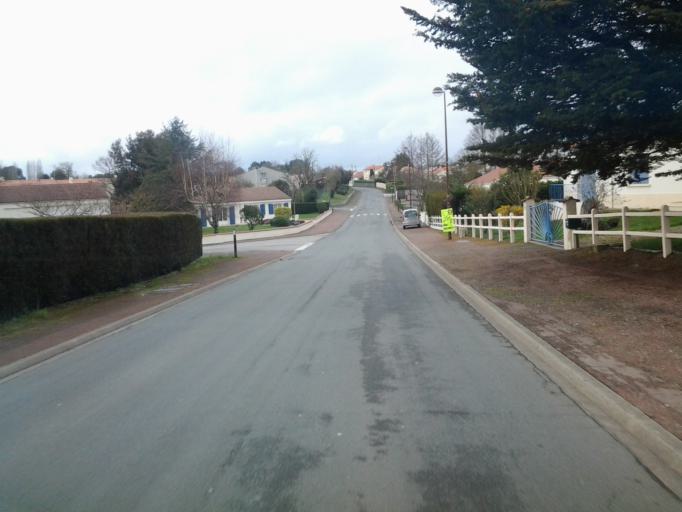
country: FR
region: Pays de la Loire
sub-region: Departement de la Vendee
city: Avrille
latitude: 46.4647
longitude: -1.4893
